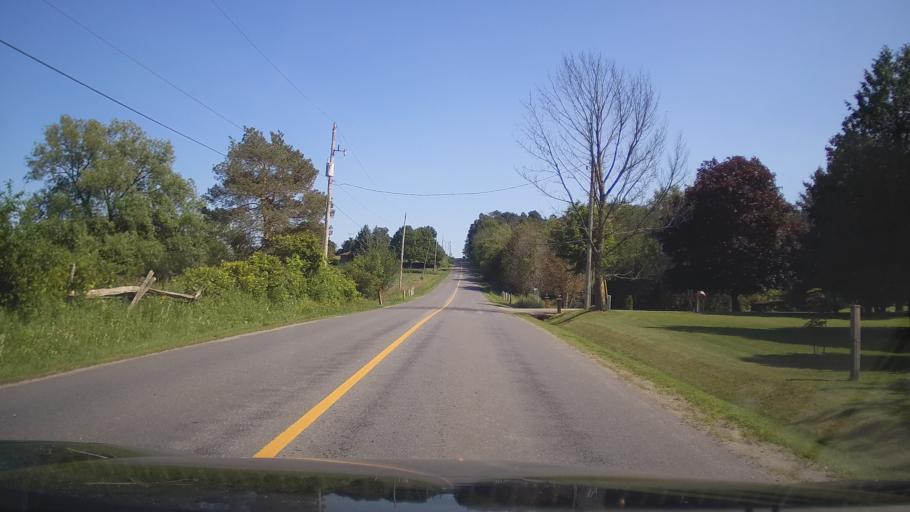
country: CA
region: Ontario
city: Oshawa
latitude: 43.9534
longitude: -78.7269
